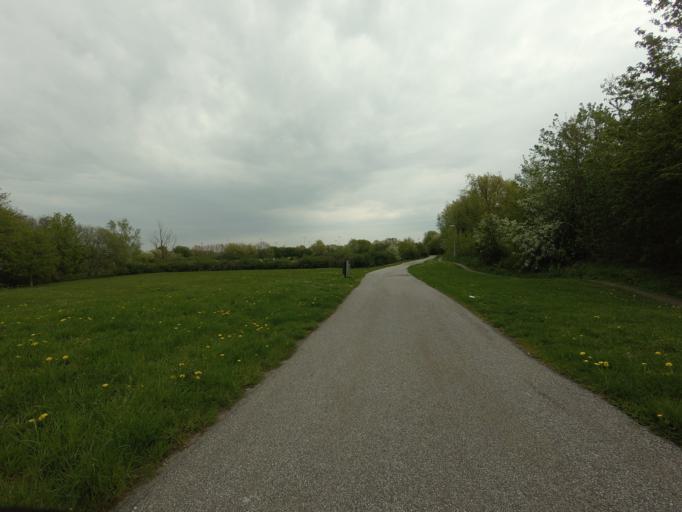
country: SE
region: Skane
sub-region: Malmo
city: Tygelsjo
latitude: 55.5541
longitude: 13.0058
